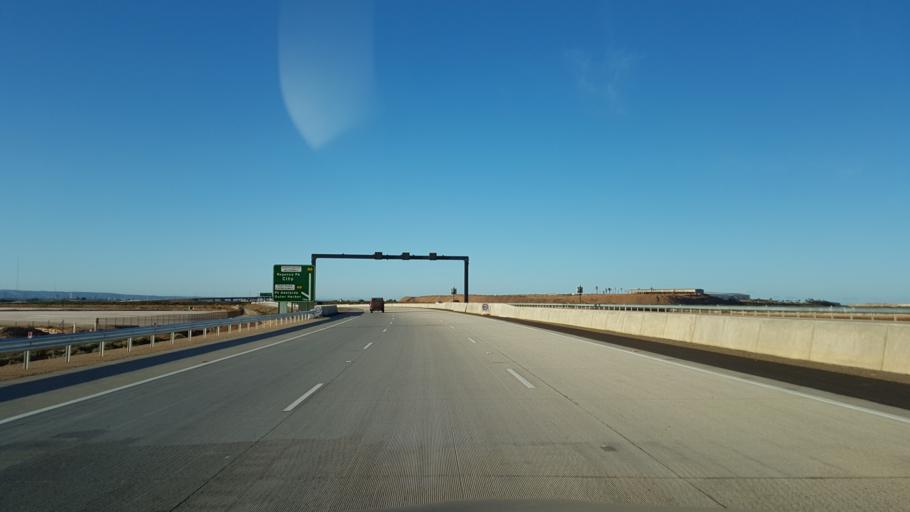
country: AU
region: South Australia
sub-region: Port Adelaide Enfield
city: Enfield
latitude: -34.8159
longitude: 138.5621
